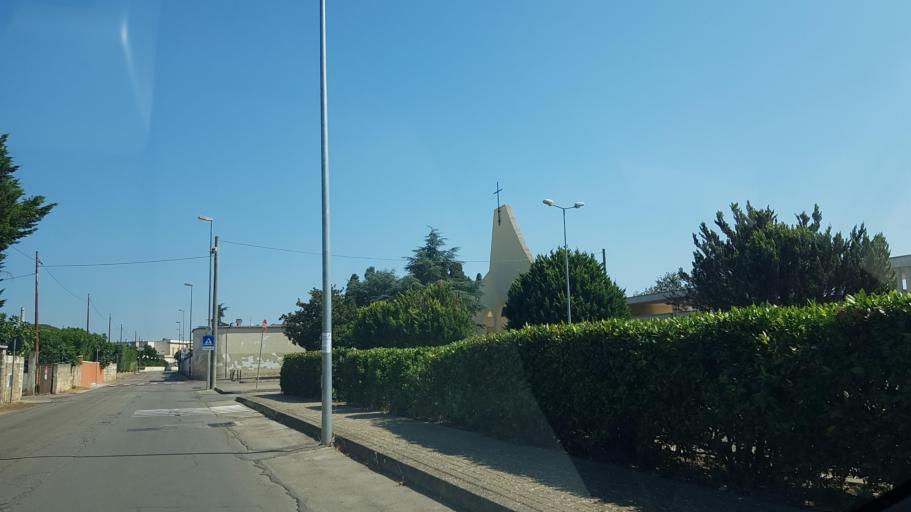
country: IT
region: Apulia
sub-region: Provincia di Lecce
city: Taurisano
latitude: 39.9613
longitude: 18.2103
